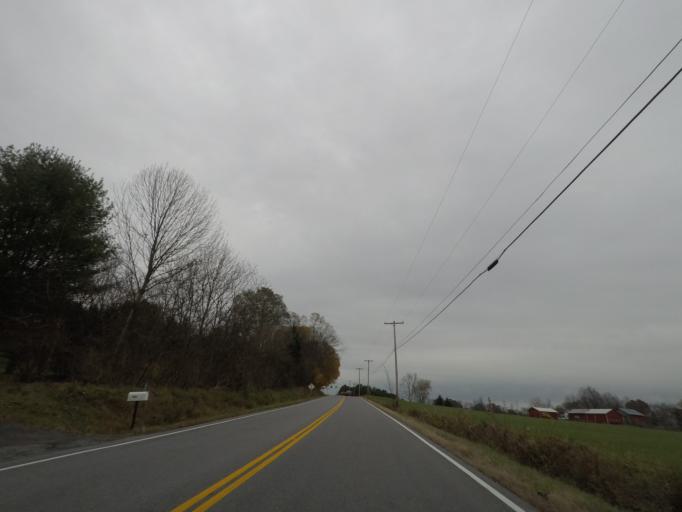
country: US
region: New York
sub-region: Schenectady County
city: East Glenville
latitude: 42.8964
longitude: -73.8734
